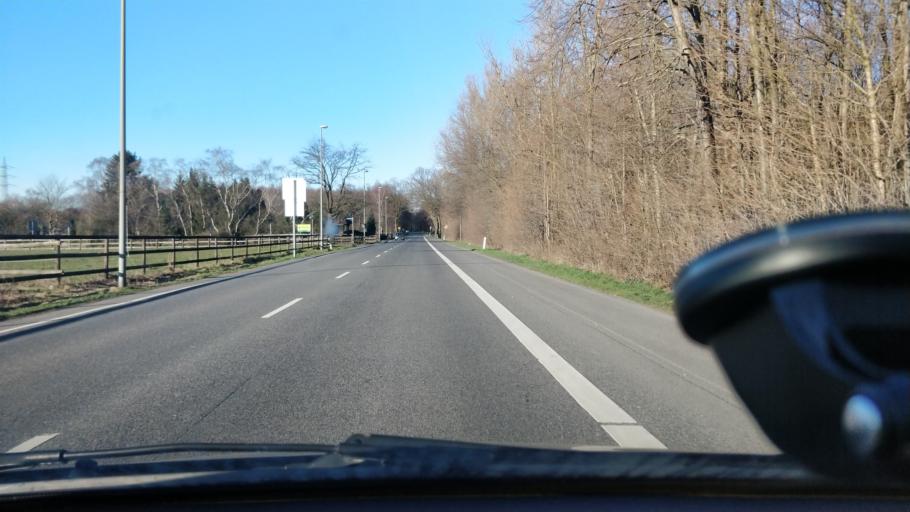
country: DE
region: North Rhine-Westphalia
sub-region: Regierungsbezirk Munster
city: Bottrop
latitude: 51.5493
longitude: 6.8690
